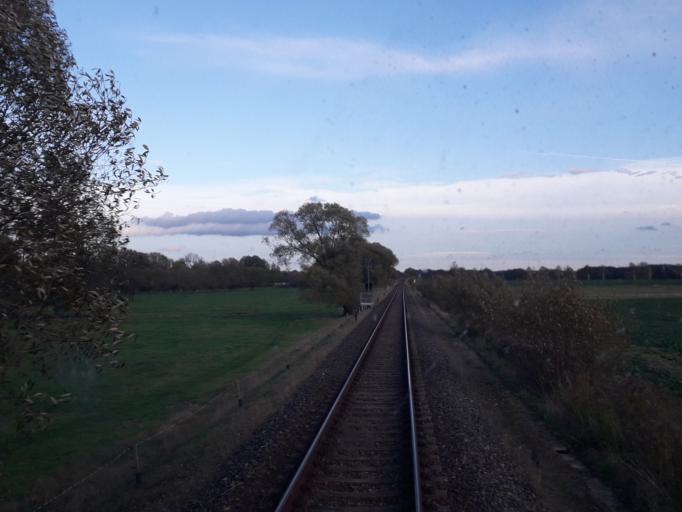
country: DE
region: Brandenburg
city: Pritzwalk
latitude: 53.1478
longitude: 12.2142
